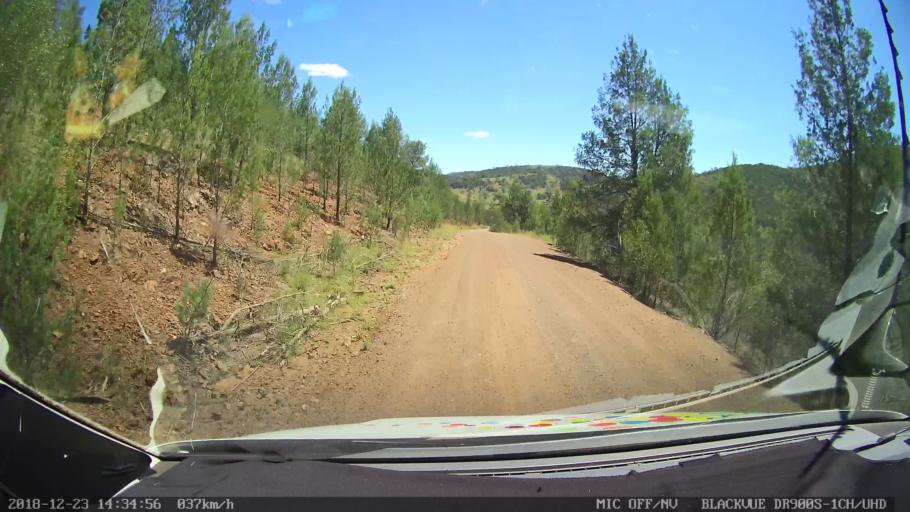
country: AU
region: New South Wales
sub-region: Tamworth Municipality
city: Manilla
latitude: -30.6076
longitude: 150.9087
